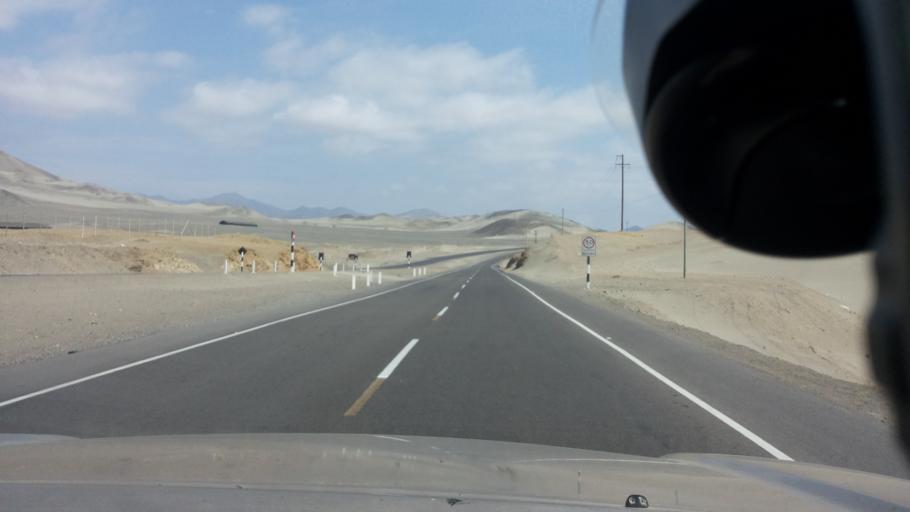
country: PE
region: Ancash
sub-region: Provincia de Huarmey
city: Huarmey
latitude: -10.0113
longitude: -78.1762
